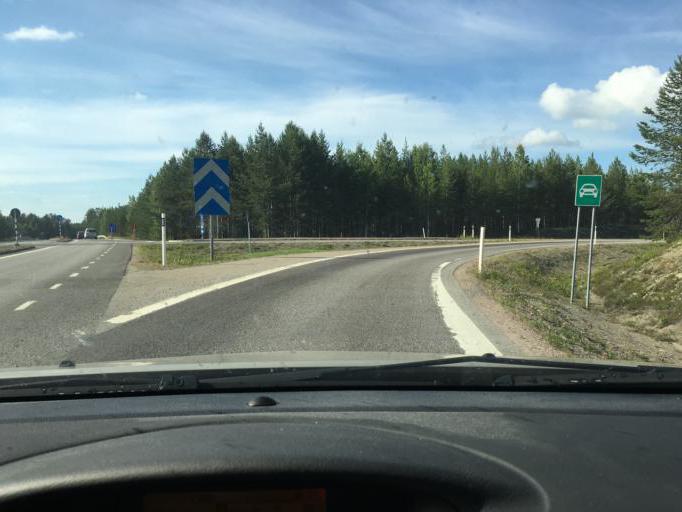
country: SE
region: Norrbotten
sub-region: Lulea Kommun
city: Gammelstad
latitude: 65.5966
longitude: 22.0470
